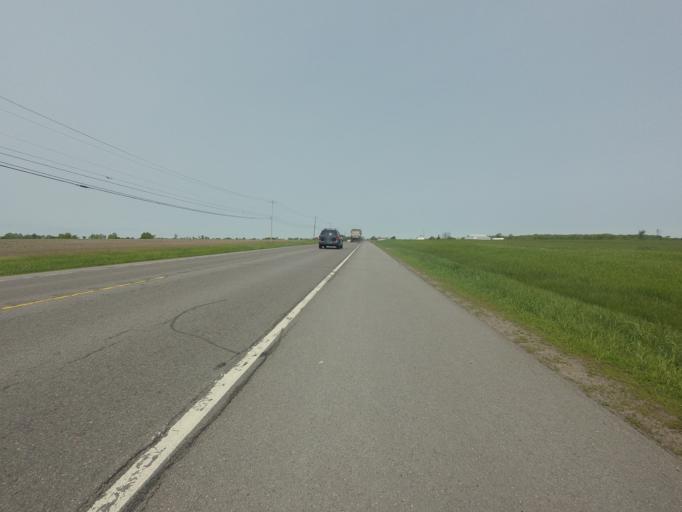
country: US
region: New York
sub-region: Jefferson County
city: Dexter
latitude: 44.0546
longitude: -76.1071
